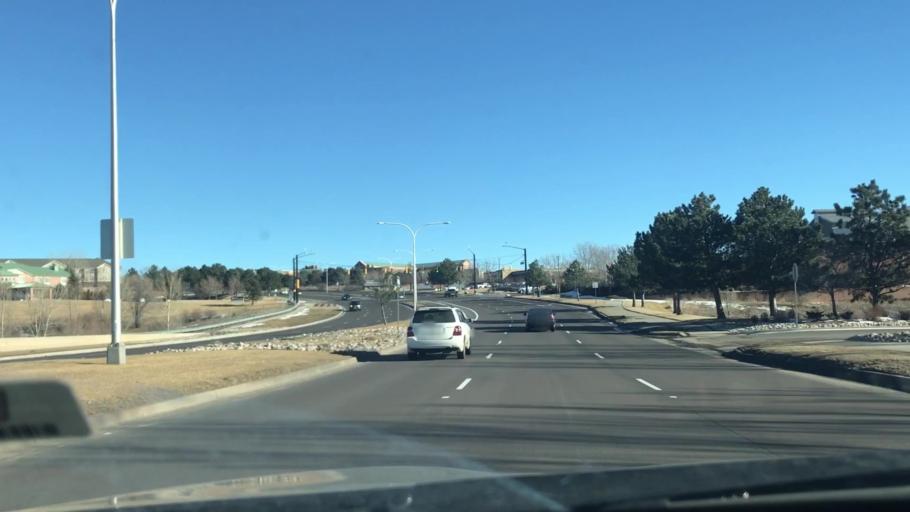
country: US
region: Colorado
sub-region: El Paso County
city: Air Force Academy
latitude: 38.9655
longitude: -104.7972
